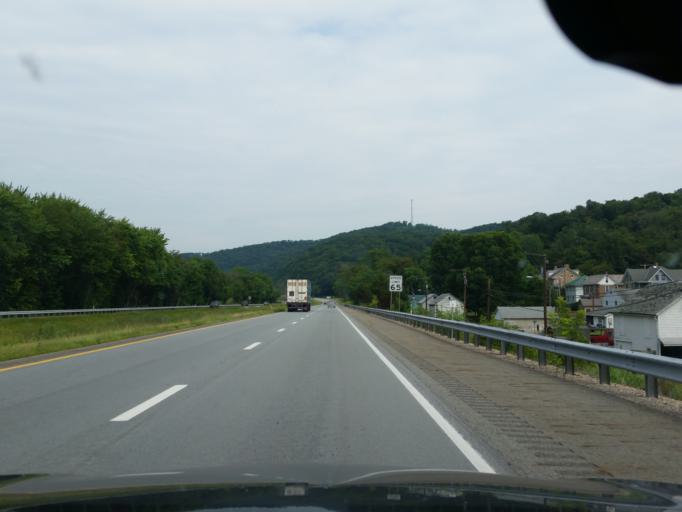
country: US
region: Pennsylvania
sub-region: Perry County
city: Newport
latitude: 40.5516
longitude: -77.1576
